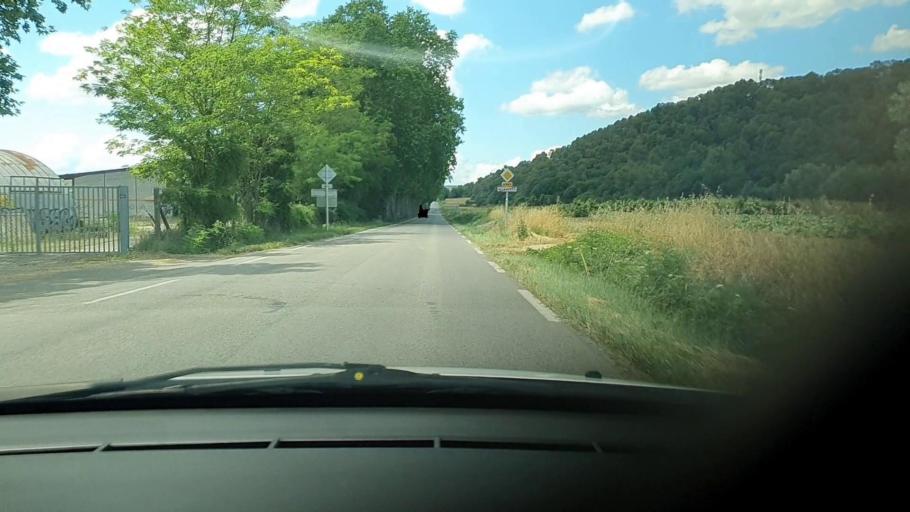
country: FR
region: Languedoc-Roussillon
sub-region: Departement du Gard
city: Montaren-et-Saint-Mediers
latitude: 44.0309
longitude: 4.3729
